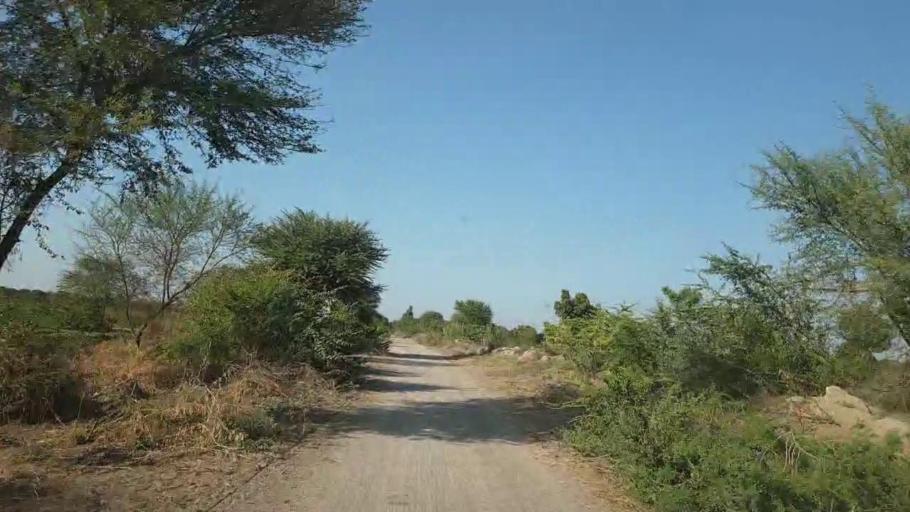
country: PK
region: Sindh
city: Kunri
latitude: 25.0610
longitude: 69.4420
